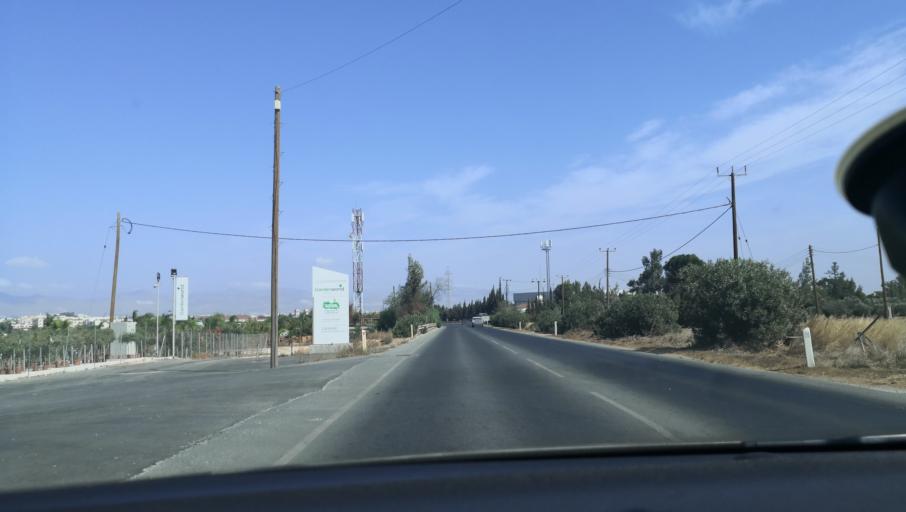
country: CY
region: Lefkosia
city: Kato Deftera
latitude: 35.0957
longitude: 33.2843
